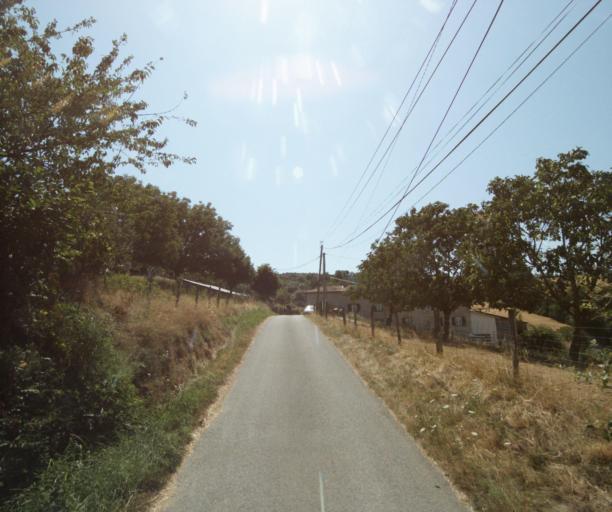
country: FR
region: Rhone-Alpes
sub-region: Departement du Rhone
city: Sourcieux-les-Mines
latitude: 45.7954
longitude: 4.6347
